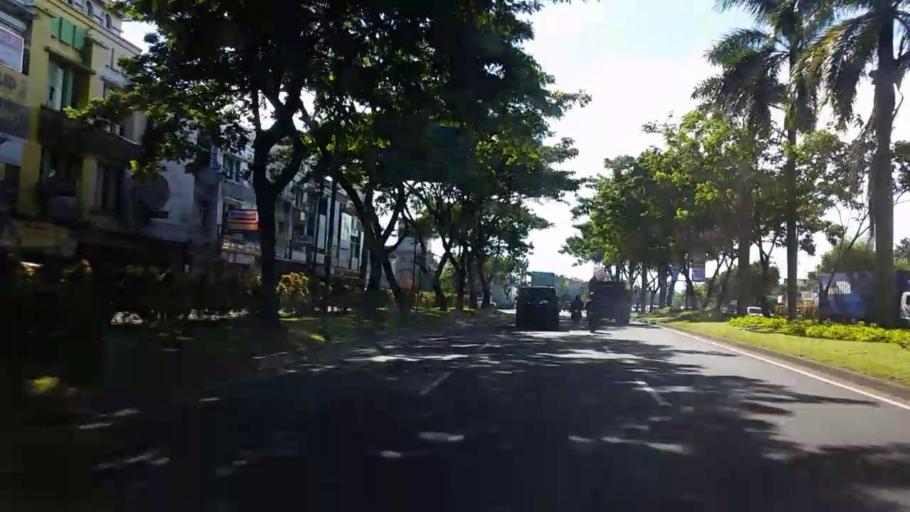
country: ID
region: West Java
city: Serpong
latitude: -6.3072
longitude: 106.6723
